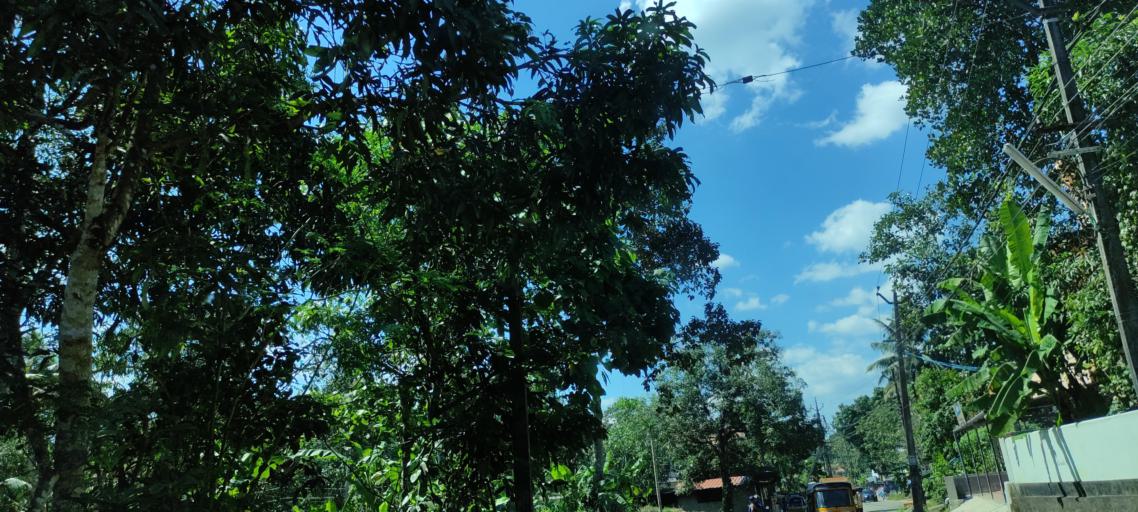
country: IN
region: Kerala
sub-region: Pattanamtitta
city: Adur
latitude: 9.0905
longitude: 76.6926
